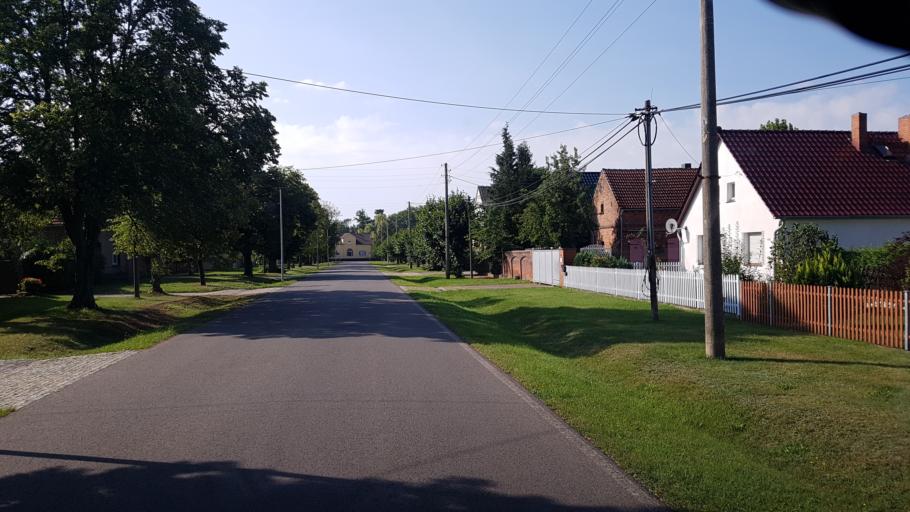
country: DE
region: Brandenburg
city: Luebben
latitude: 51.8684
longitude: 13.8569
